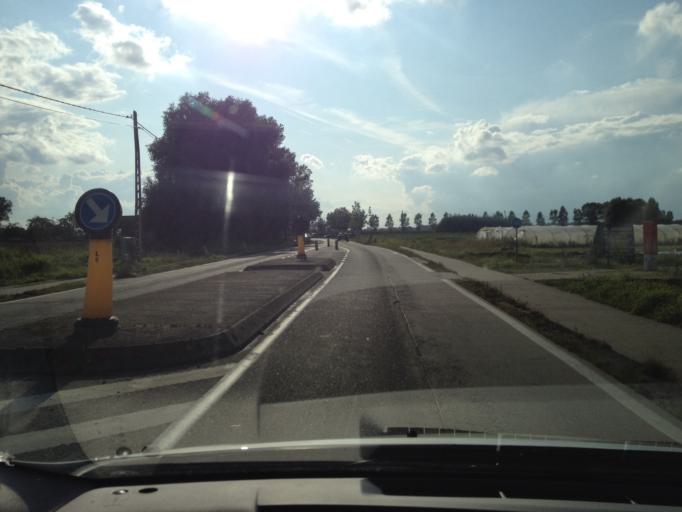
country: BE
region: Flanders
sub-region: Provincie West-Vlaanderen
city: Ichtegem
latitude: 51.1208
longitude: 3.0280
